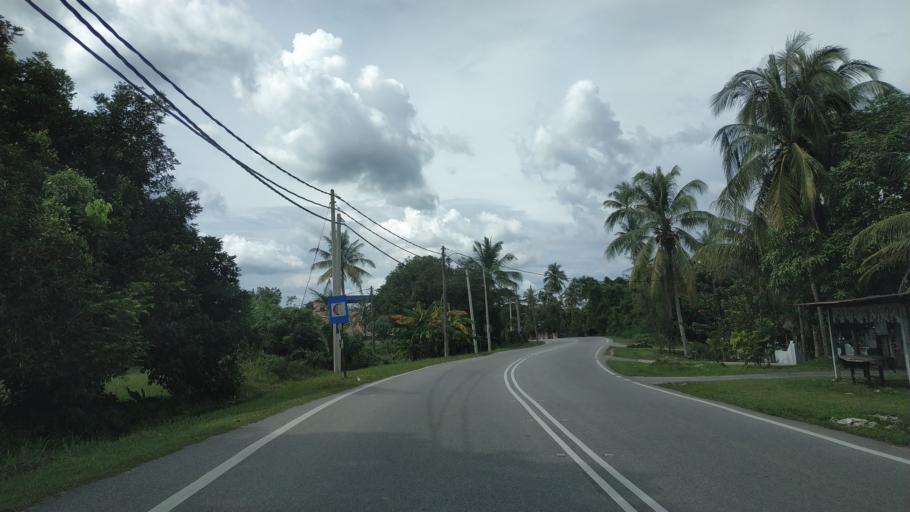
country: MY
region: Kedah
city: Kulim
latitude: 5.4241
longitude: 100.6641
